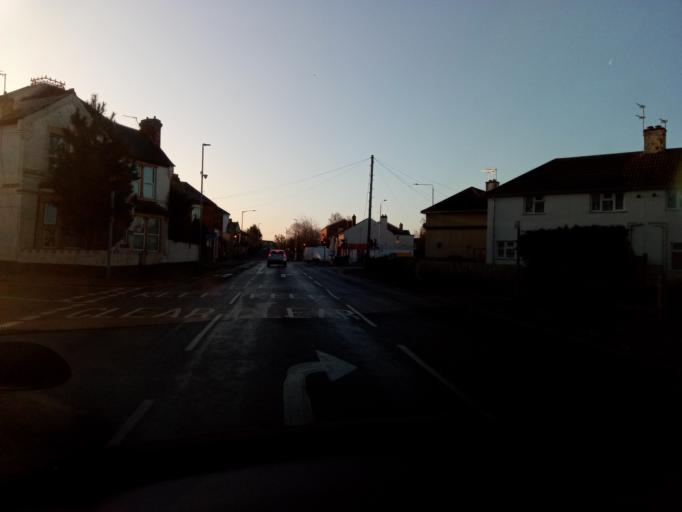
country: GB
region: England
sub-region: Leicestershire
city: Loughborough
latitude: 52.7803
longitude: -1.2018
